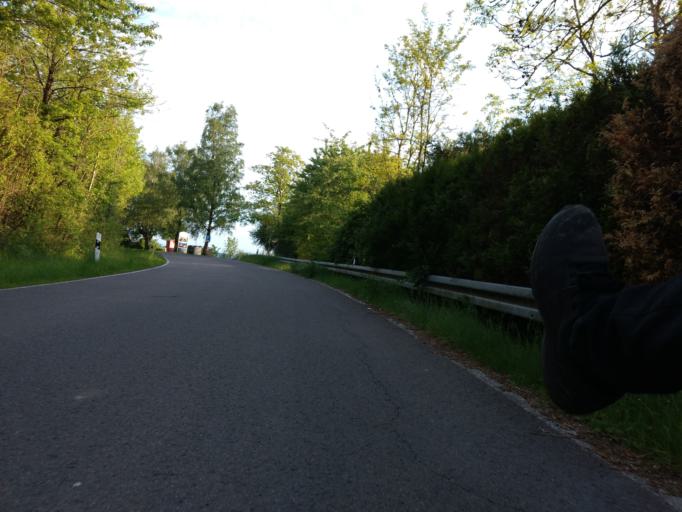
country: DE
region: Saarland
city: Beckingen
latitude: 49.4055
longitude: 6.6641
